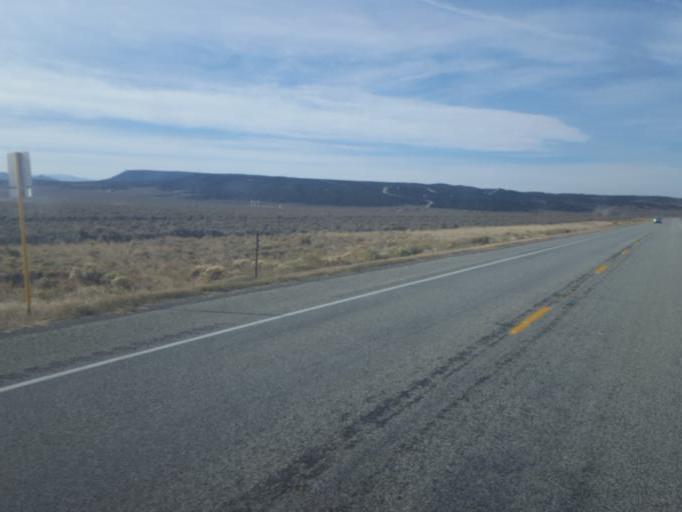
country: US
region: Colorado
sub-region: Costilla County
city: San Luis
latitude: 37.4420
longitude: -105.3816
